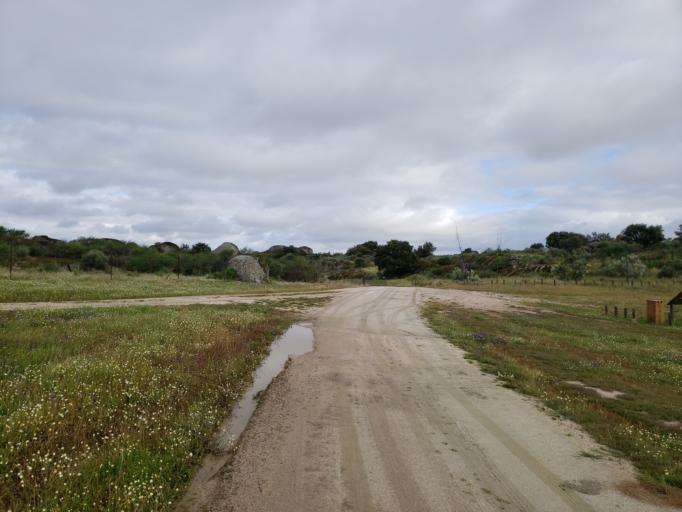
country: ES
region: Extremadura
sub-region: Provincia de Caceres
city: Malpartida de Caceres
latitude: 39.4248
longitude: -6.4874
